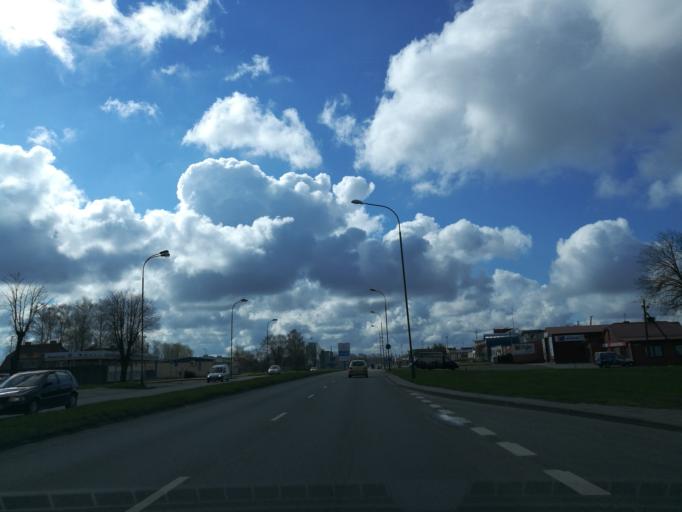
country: LT
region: Klaipedos apskritis
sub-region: Klaipeda
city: Klaipeda
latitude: 55.6919
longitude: 21.1428
